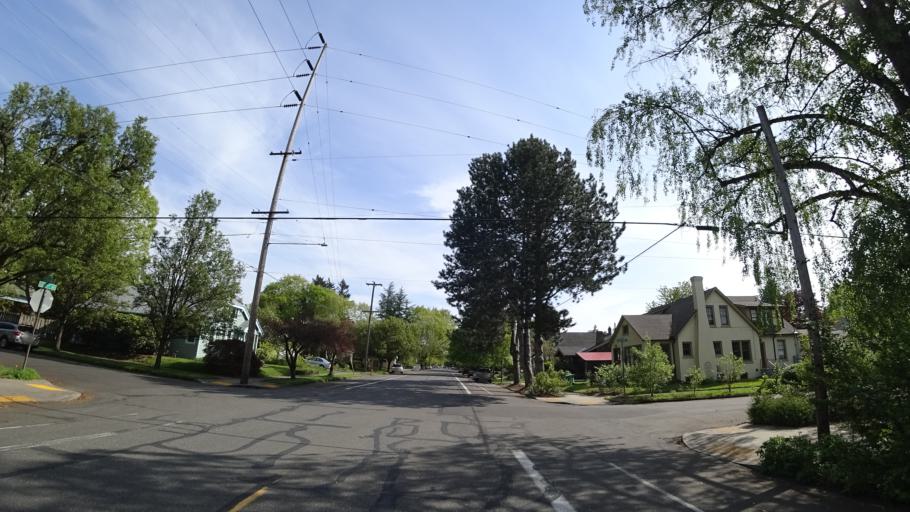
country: US
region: Oregon
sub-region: Clackamas County
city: Milwaukie
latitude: 45.4816
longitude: -122.6206
